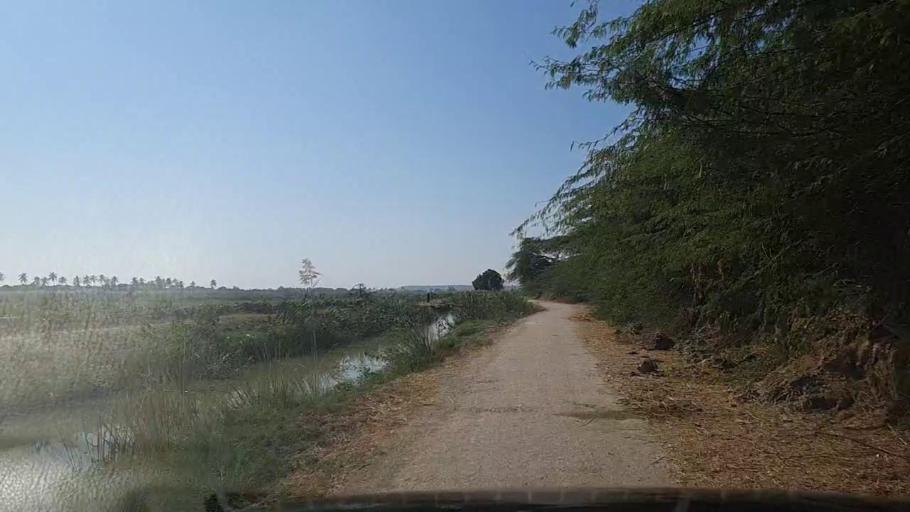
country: PK
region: Sindh
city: Thatta
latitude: 24.6368
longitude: 67.8753
